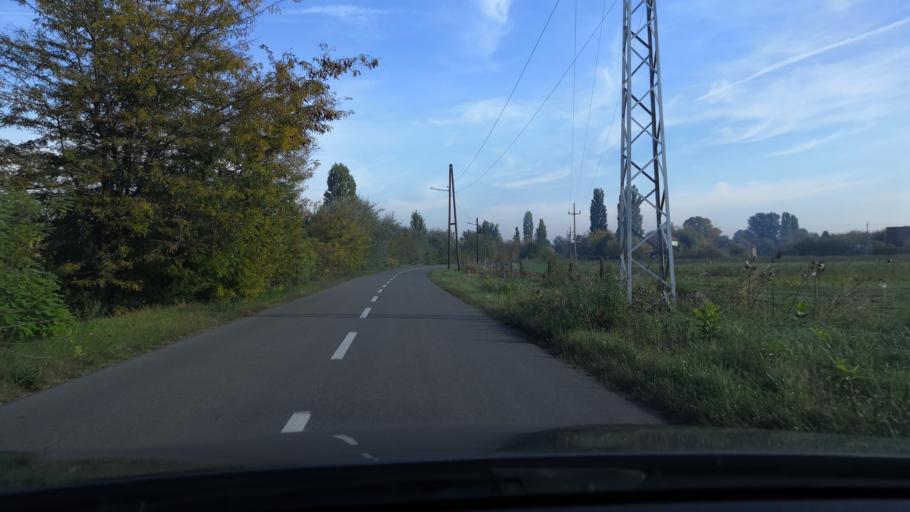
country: HU
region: Csongrad
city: Asotthalom
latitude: 46.1229
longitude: 19.8474
